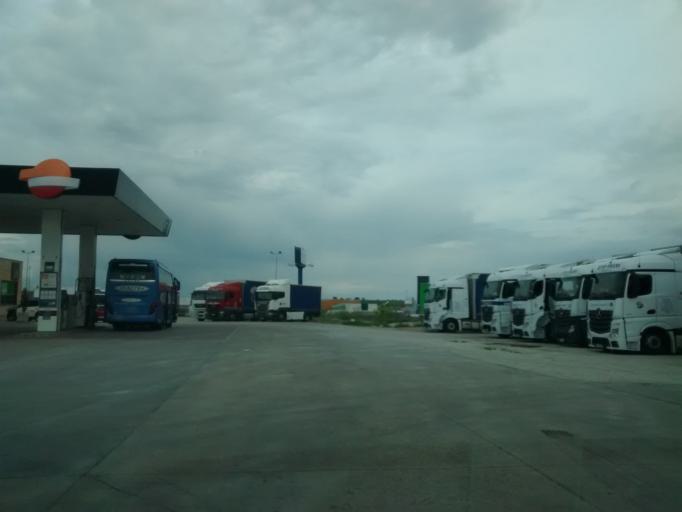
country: ES
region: Castille-La Mancha
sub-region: Provincia de Guadalajara
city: Torija
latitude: 40.7481
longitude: -3.0332
